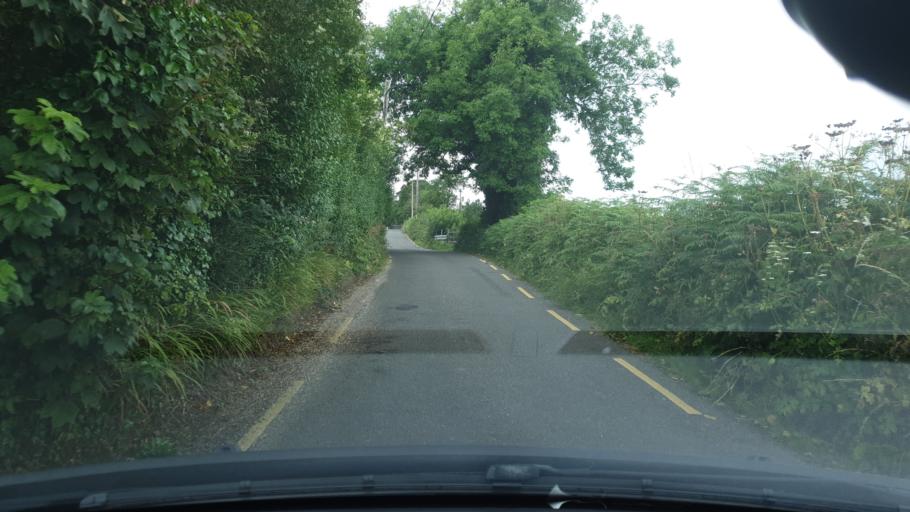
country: IE
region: Munster
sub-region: Ciarrai
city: Tralee
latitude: 52.2419
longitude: -9.6460
